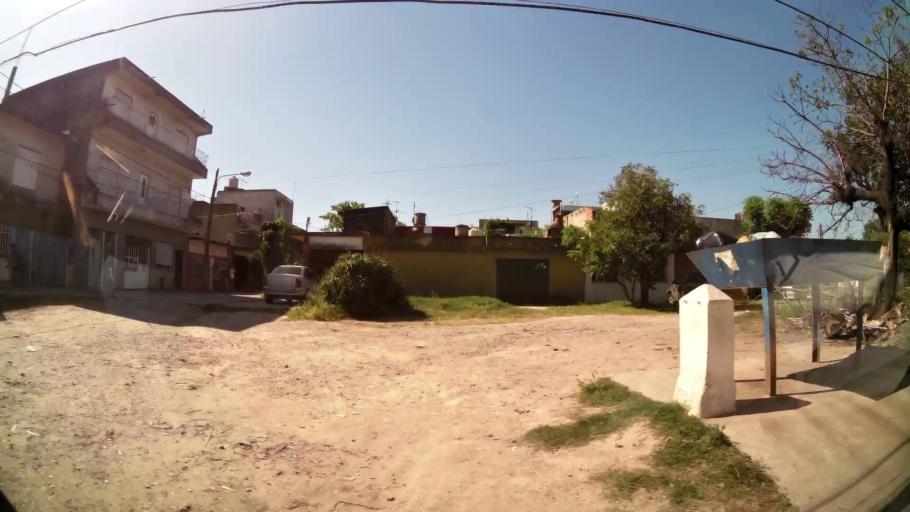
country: AR
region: Buenos Aires F.D.
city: Villa Lugano
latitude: -34.7049
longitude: -58.4724
